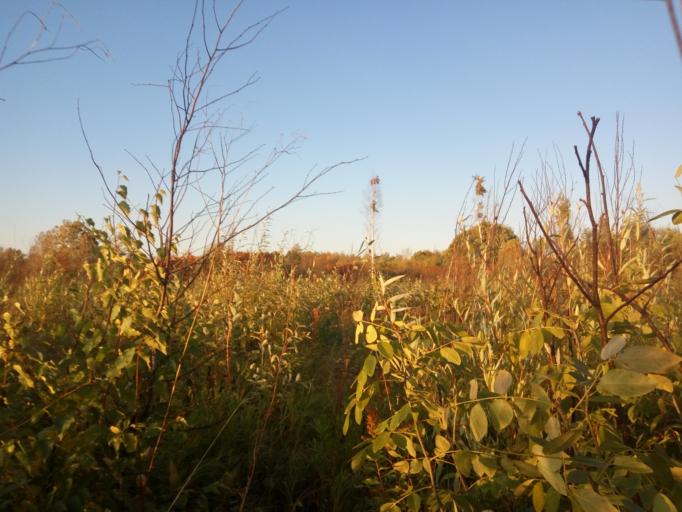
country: RU
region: Khabarovsk Krai
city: Khor
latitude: 47.7040
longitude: 134.9644
